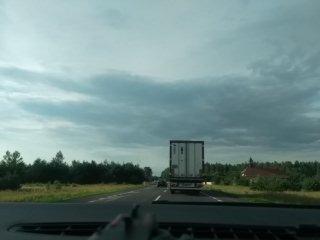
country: PL
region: Subcarpathian Voivodeship
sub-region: Powiat nizanski
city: Jarocin
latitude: 50.6358
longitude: 22.2865
